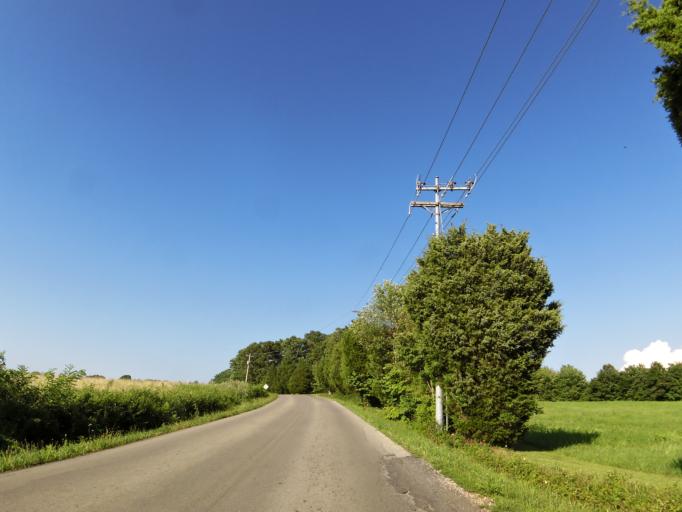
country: US
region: Tennessee
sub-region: Blount County
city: Maryville
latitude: 35.7240
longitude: -83.9264
